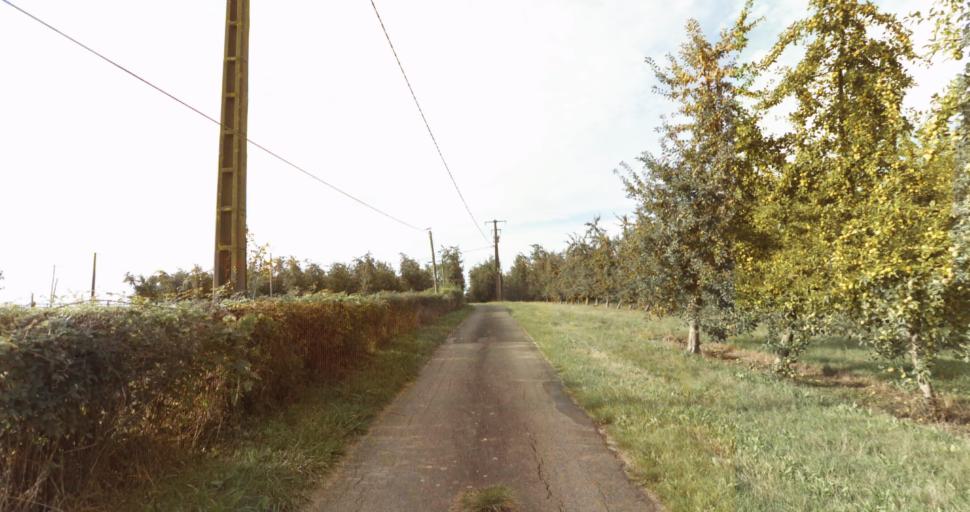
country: FR
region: Lower Normandy
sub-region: Departement de l'Orne
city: Gace
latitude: 48.6967
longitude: 0.3141
